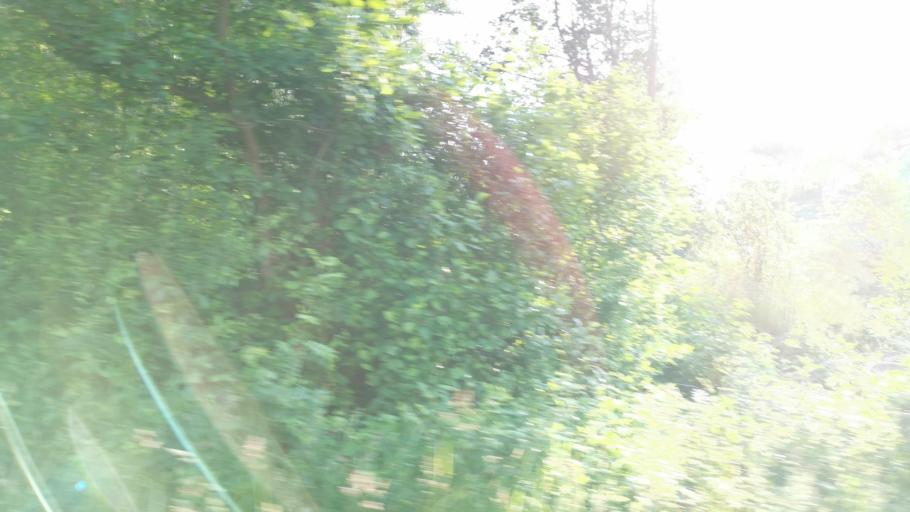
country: SE
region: Vaestra Goetaland
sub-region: Orust
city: Henan
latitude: 58.2893
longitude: 11.6476
